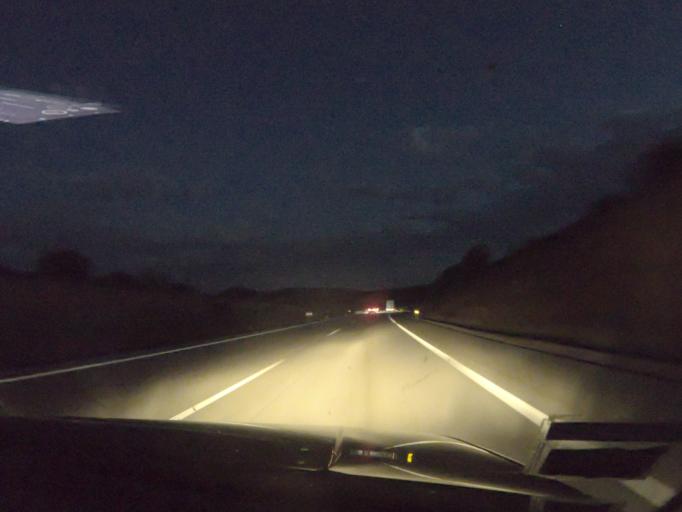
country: ES
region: Castille and Leon
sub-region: Provincia de Leon
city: Brazuelo
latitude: 42.5179
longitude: -6.1189
